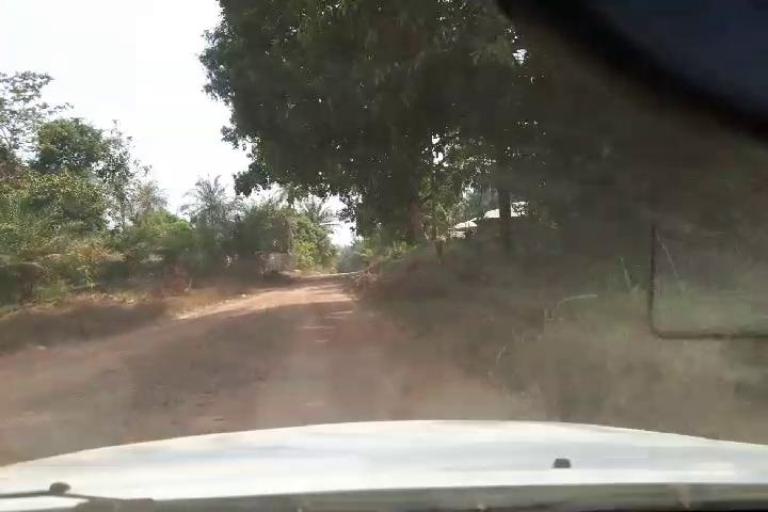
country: SL
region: Northern Province
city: Masingbi
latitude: 8.7902
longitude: -11.8701
